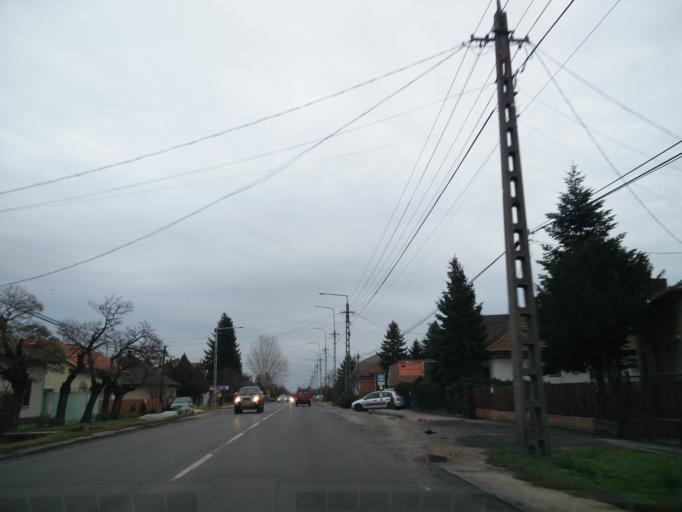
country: HU
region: Pest
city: Ullo
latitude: 47.3890
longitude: 19.3285
